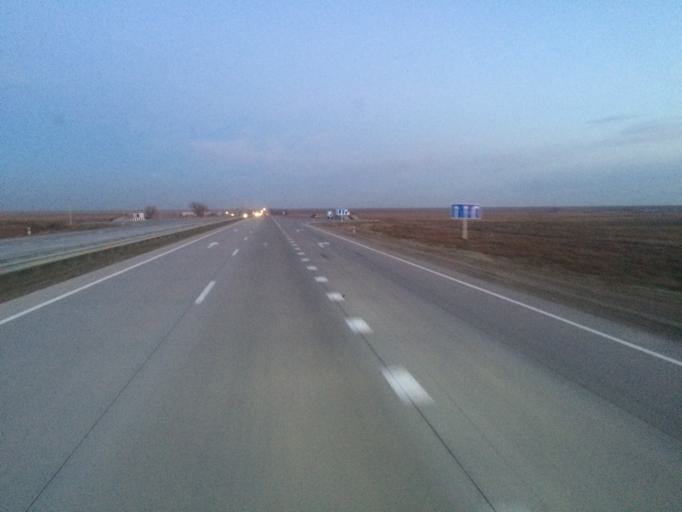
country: KZ
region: Ongtustik Qazaqstan
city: Temirlanovka
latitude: 42.8466
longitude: 69.0921
